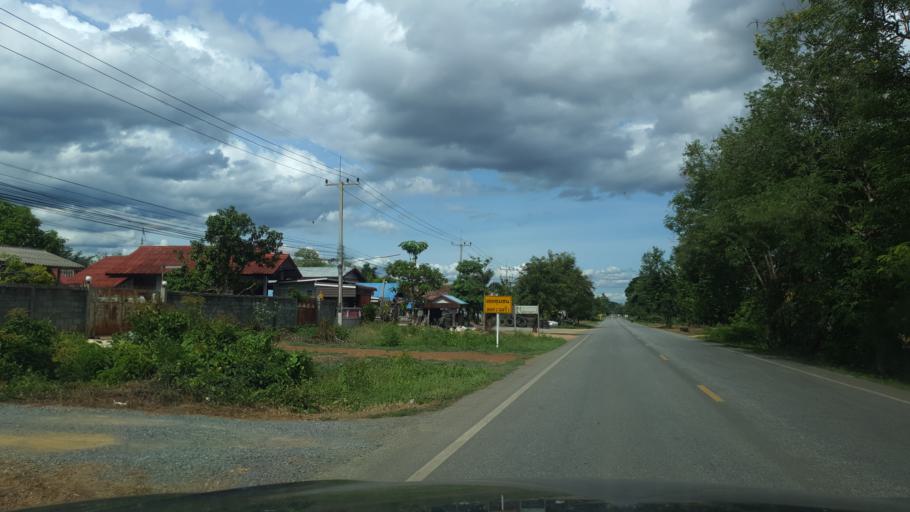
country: TH
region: Sukhothai
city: Thung Saliam
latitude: 17.3350
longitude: 99.5598
